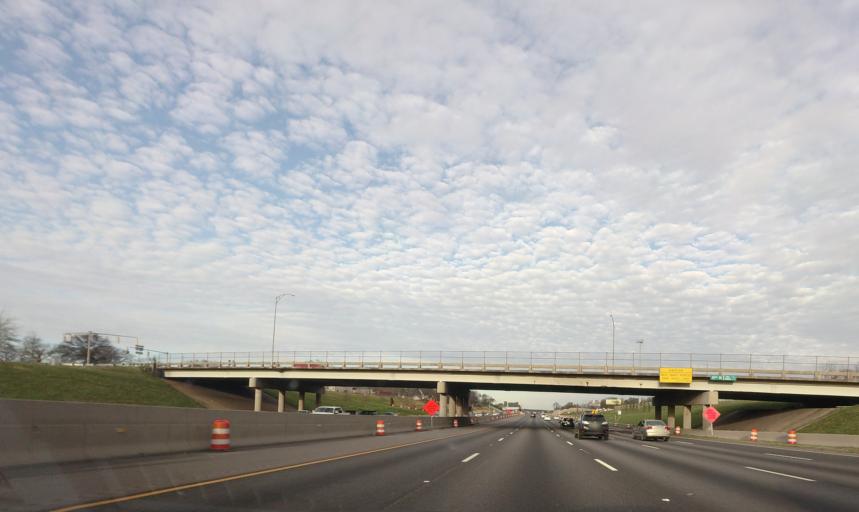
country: US
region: Alabama
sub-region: Jefferson County
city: Birmingham
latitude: 33.5326
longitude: -86.7986
